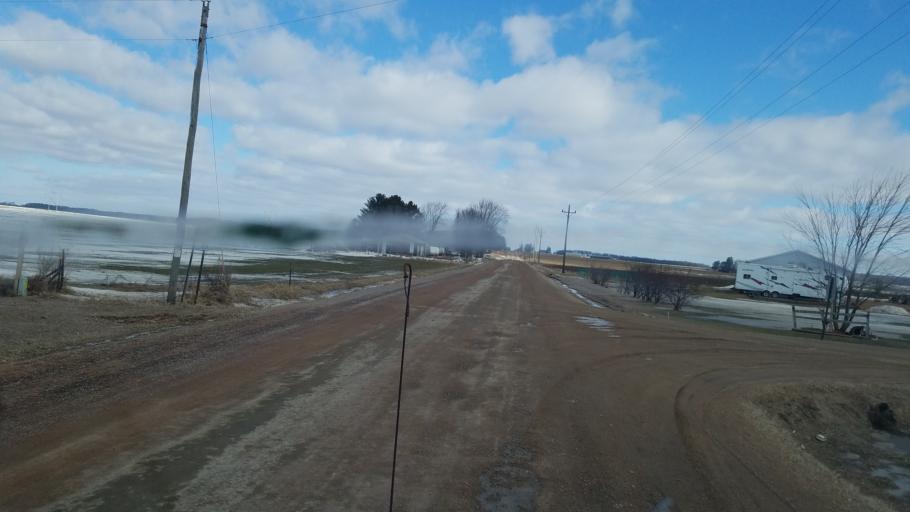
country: US
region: Wisconsin
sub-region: Clark County
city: Loyal
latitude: 44.6615
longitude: -90.4356
